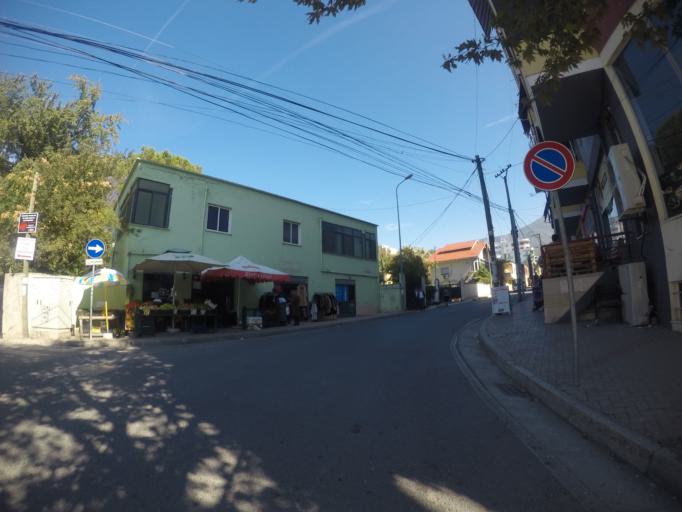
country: AL
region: Tirane
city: Tirana
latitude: 41.3472
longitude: 19.8558
